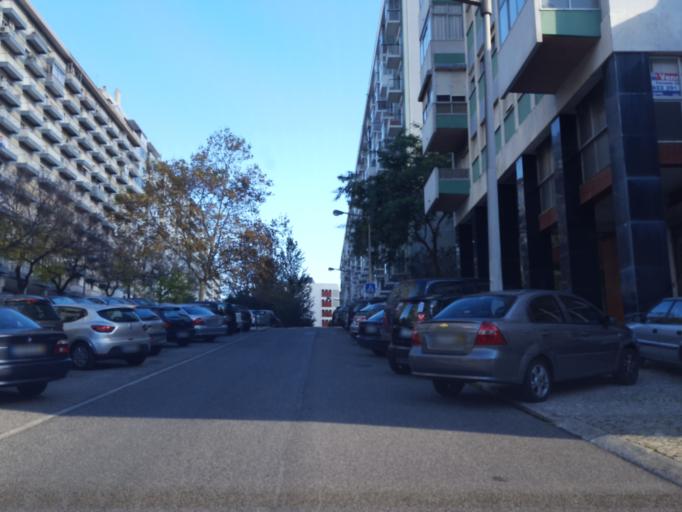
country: PT
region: Lisbon
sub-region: Odivelas
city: Pontinha
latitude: 38.7477
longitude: -9.1878
